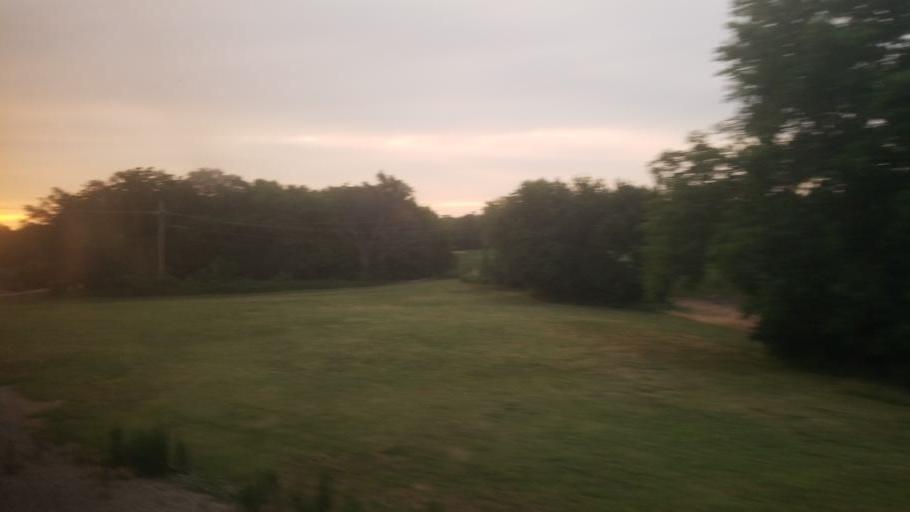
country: US
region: Kansas
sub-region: Marion County
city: Peabody
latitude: 38.1615
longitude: -97.1107
